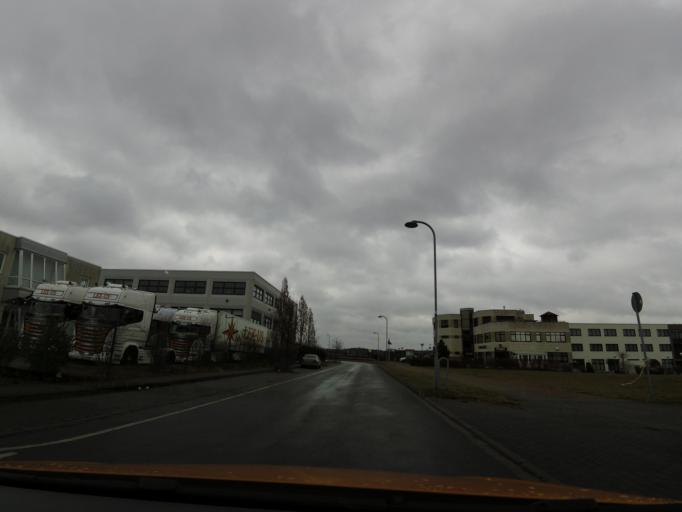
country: DE
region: Brandenburg
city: Rangsdorf
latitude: 52.3113
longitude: 13.4384
